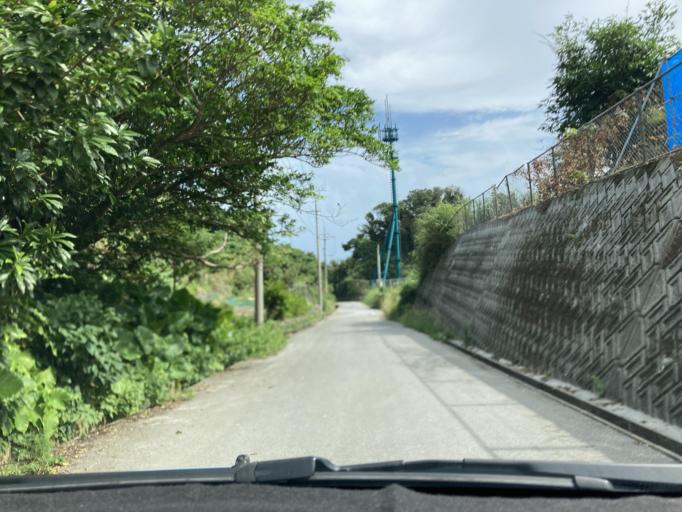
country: JP
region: Okinawa
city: Ginowan
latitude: 26.1601
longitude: 127.8107
